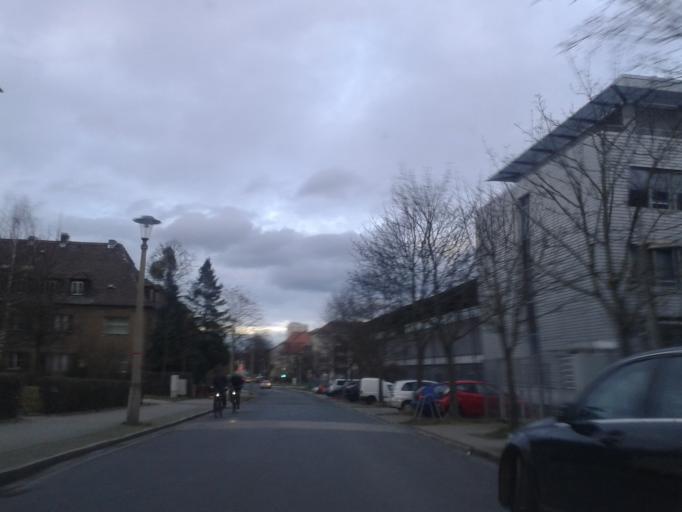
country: DE
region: Saxony
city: Dresden
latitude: 51.0297
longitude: 13.7792
